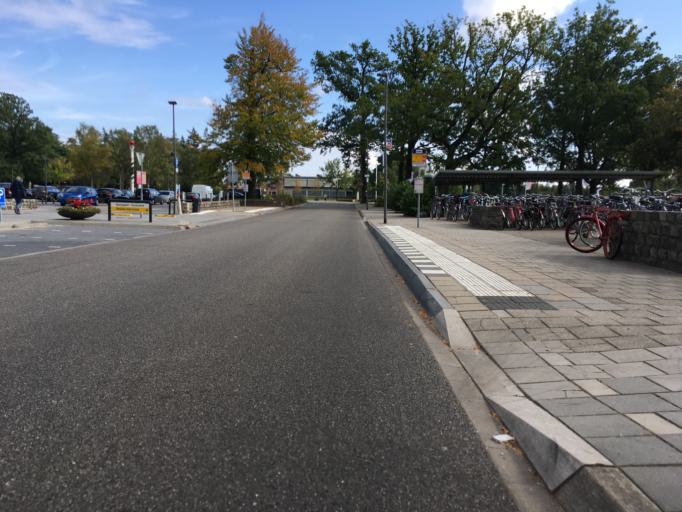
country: NL
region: Overijssel
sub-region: Gemeente Enschede
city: Enschede
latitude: 52.2396
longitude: 6.8492
